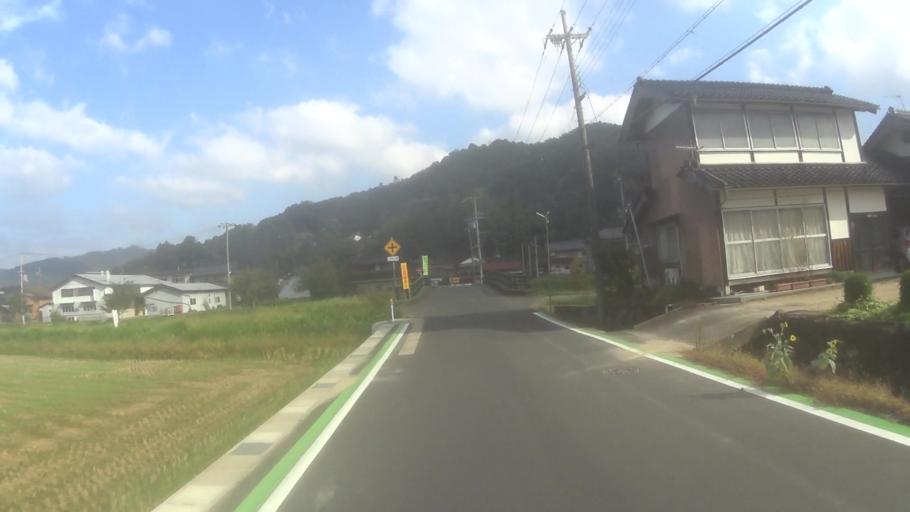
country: JP
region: Kyoto
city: Miyazu
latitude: 35.5302
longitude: 135.1258
